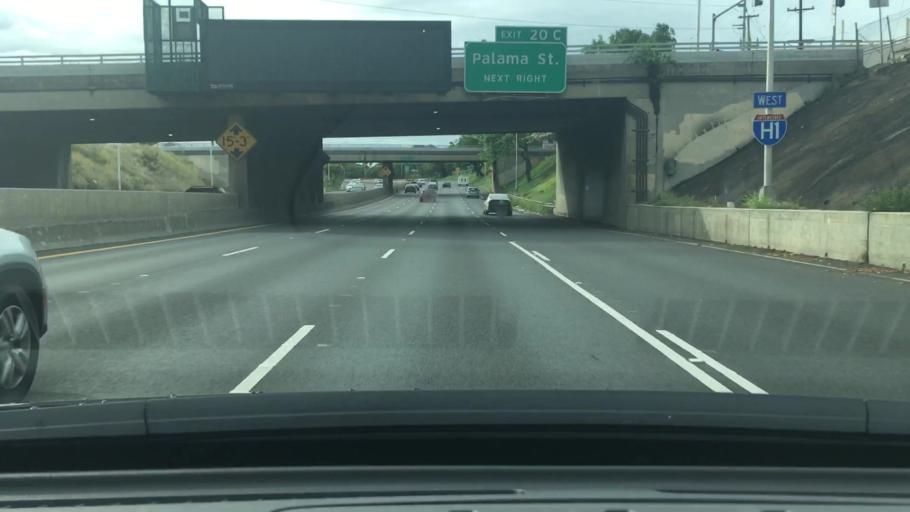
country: US
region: Hawaii
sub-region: Honolulu County
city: Honolulu
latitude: 21.3212
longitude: -157.8599
